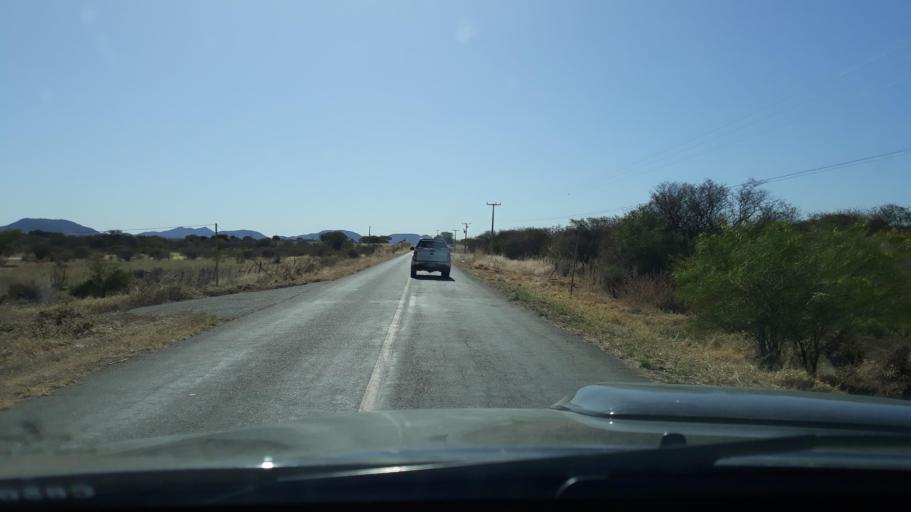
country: BR
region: Bahia
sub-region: Guanambi
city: Guanambi
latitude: -14.1095
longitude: -42.8652
